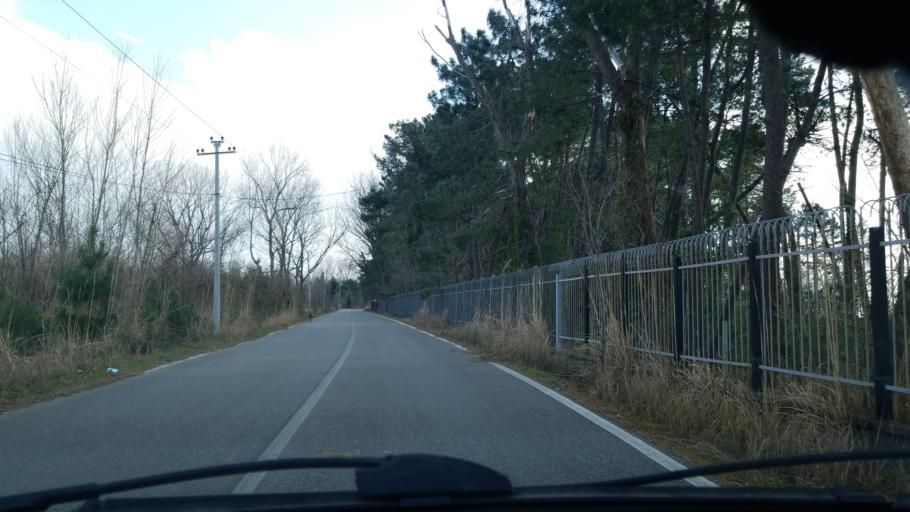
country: AL
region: Lezhe
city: Shengjin
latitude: 41.7832
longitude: 19.6033
